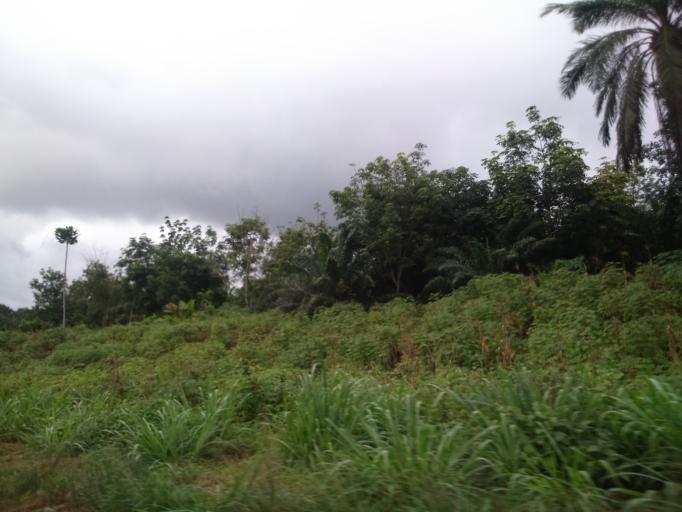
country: CI
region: Sud-Comoe
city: Adiake
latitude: 5.2996
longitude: -3.3443
